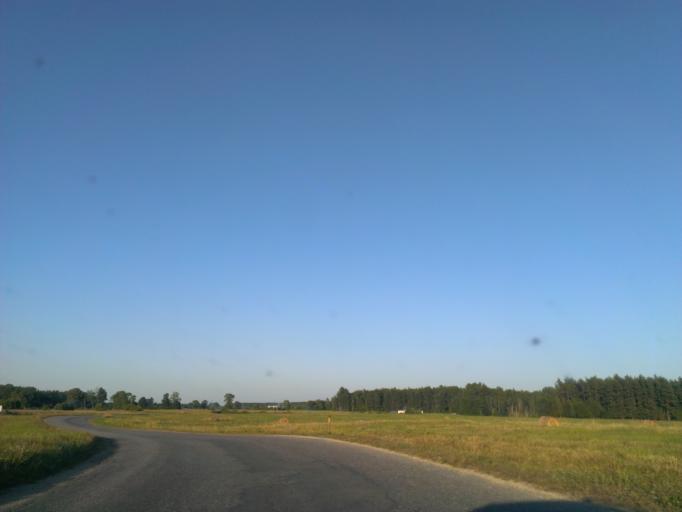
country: LV
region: Garkalne
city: Garkalne
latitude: 57.0636
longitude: 24.3815
